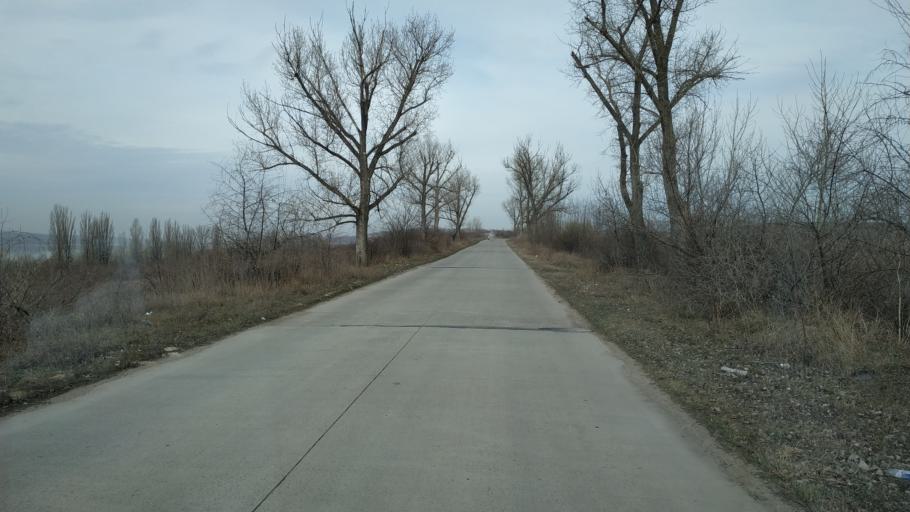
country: MD
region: Chisinau
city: Vatra
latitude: 47.0981
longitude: 28.7333
